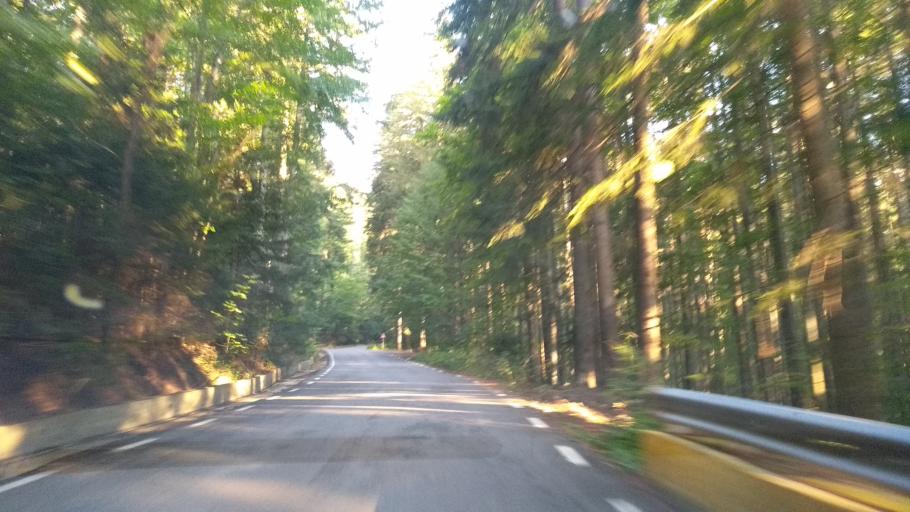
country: RO
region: Prahova
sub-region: Oras Sinaia
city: Sinaia
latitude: 45.3157
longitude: 25.5191
